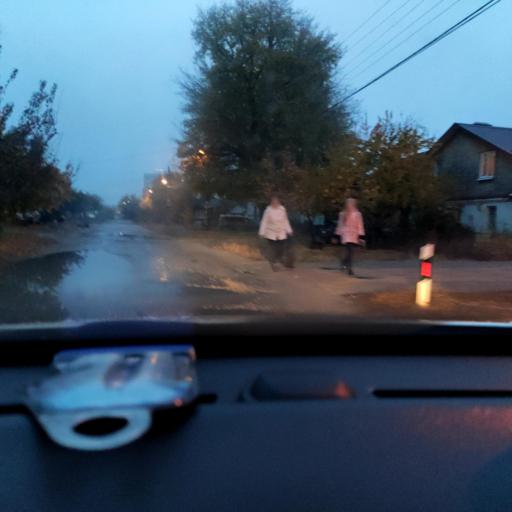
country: RU
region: Voronezj
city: Voronezh
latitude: 51.6993
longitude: 39.2663
